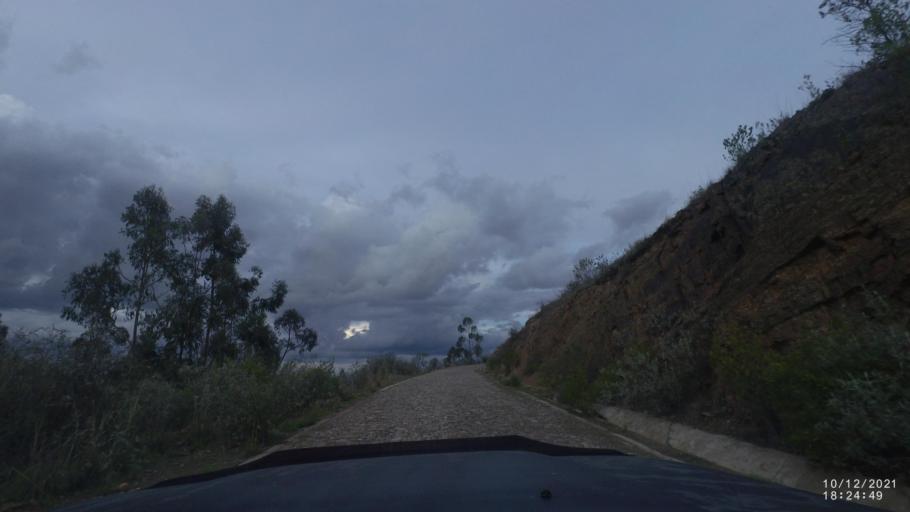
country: BO
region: Cochabamba
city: Tarata
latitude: -17.7895
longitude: -65.9743
